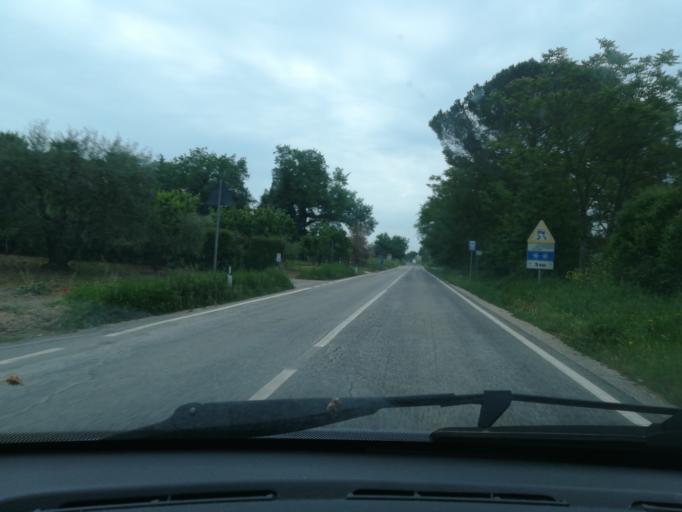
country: IT
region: The Marches
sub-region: Provincia di Macerata
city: Tolentino
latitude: 43.2651
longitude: 13.2524
